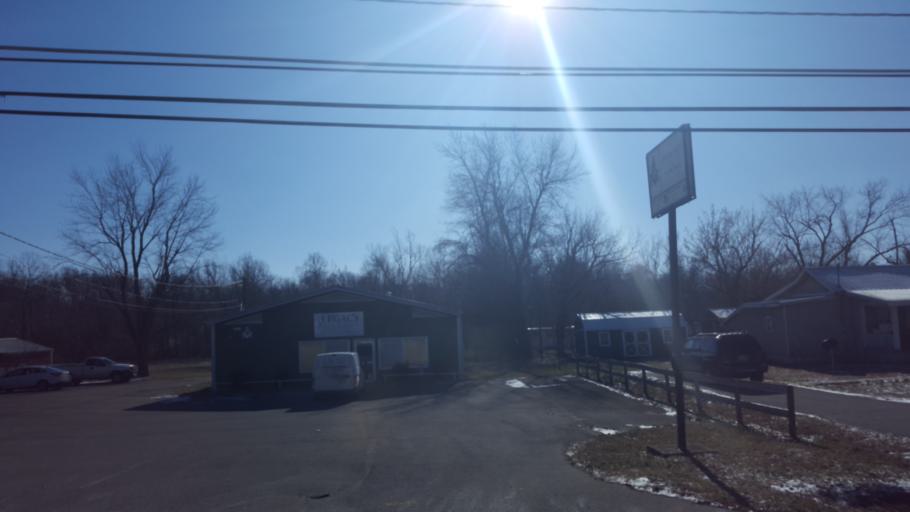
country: US
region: Kentucky
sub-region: Crittenden County
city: Marion
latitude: 37.3404
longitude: -88.0772
